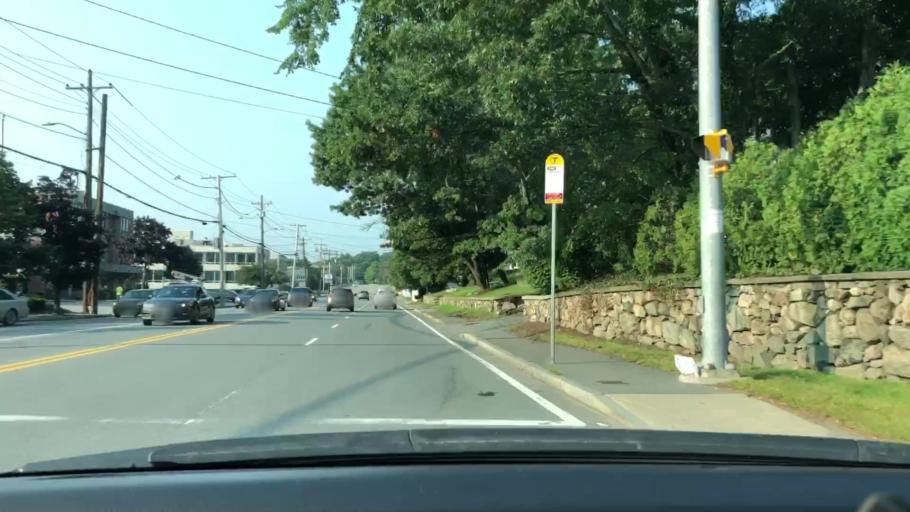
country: US
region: Massachusetts
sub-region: Norfolk County
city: Dedham
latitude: 42.2343
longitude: -71.1835
